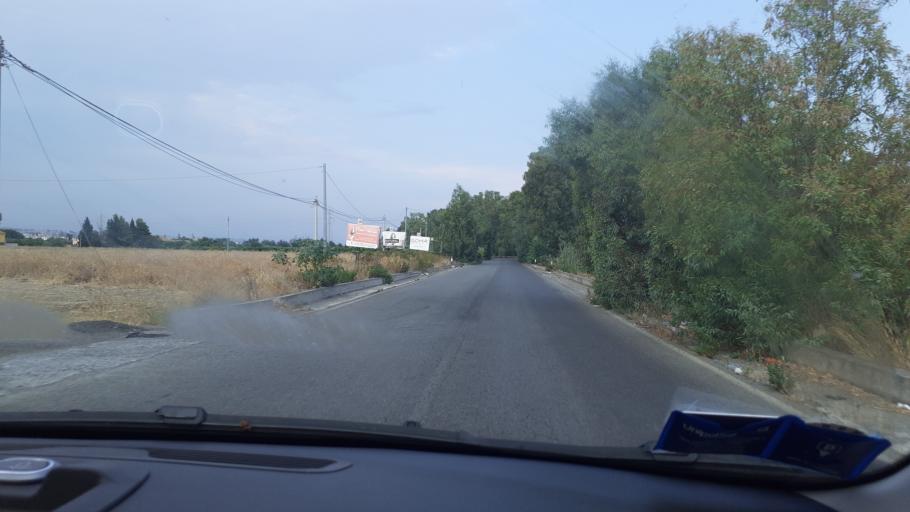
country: IT
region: Sicily
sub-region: Catania
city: Catania
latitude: 37.4494
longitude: 15.0219
